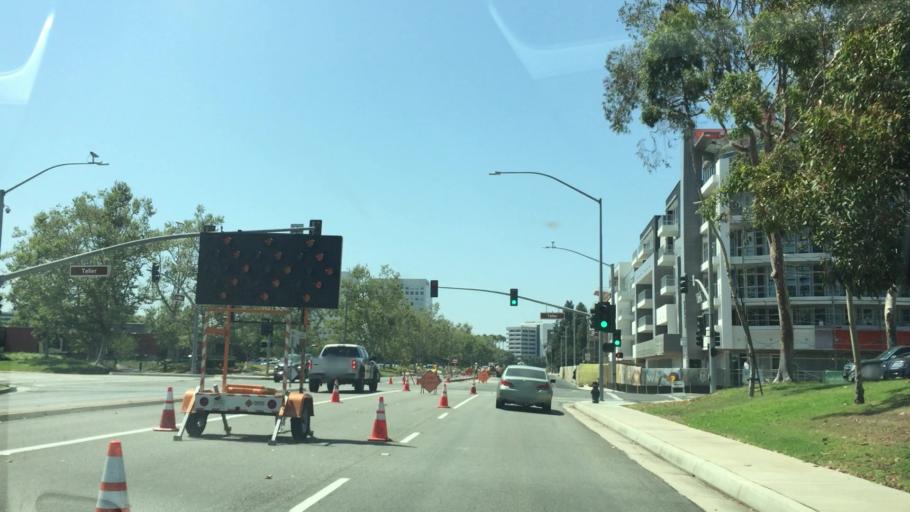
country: US
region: California
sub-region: Orange County
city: Irvine
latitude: 33.6671
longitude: -117.8555
